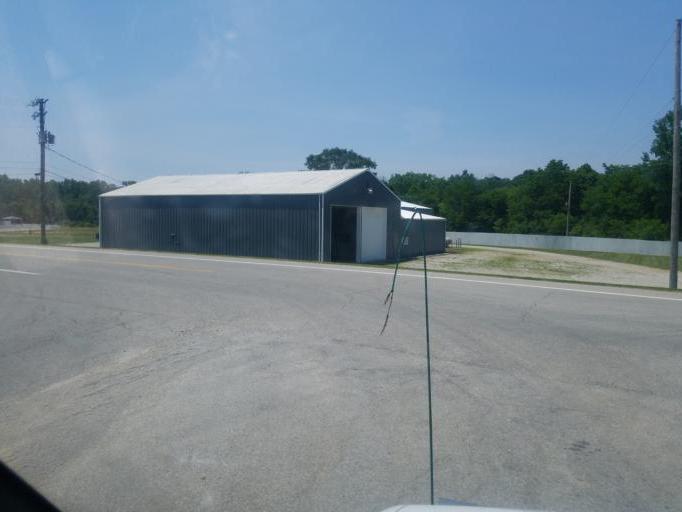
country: US
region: Ohio
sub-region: Shelby County
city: Sidney
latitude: 40.3034
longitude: -84.1386
